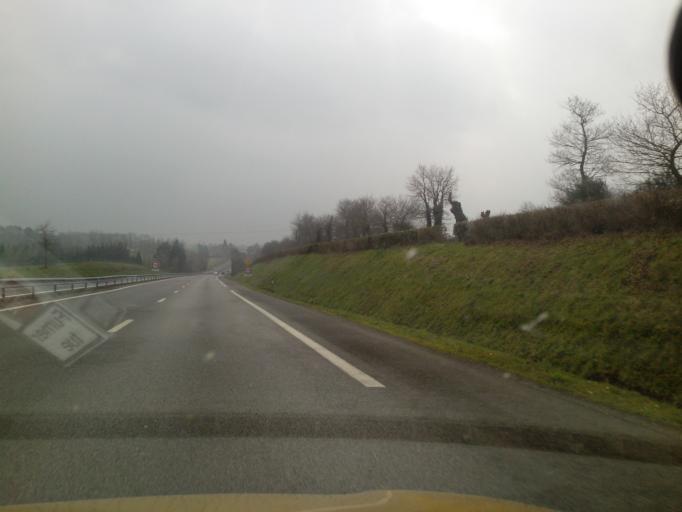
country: FR
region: Brittany
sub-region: Departement du Morbihan
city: Ploermel
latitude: 47.8961
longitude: -2.4132
